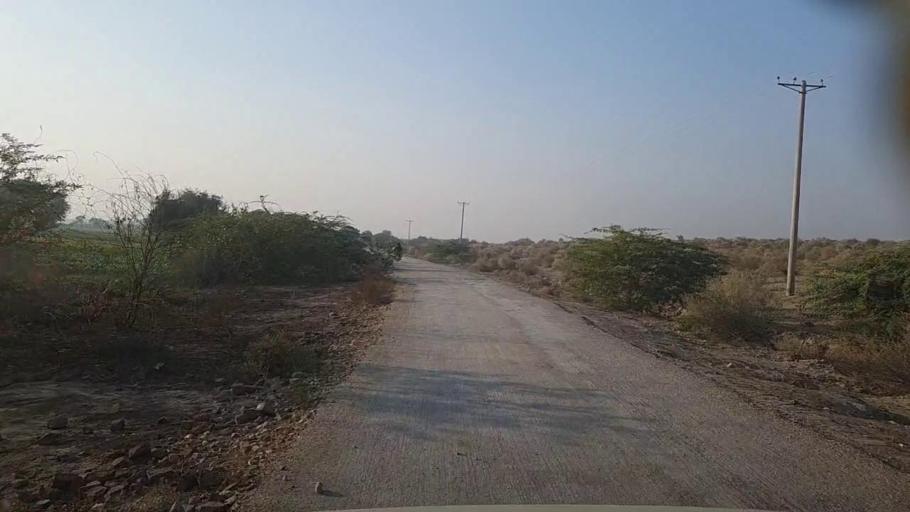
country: PK
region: Sindh
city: Pad Idan
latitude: 26.7207
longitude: 68.4547
